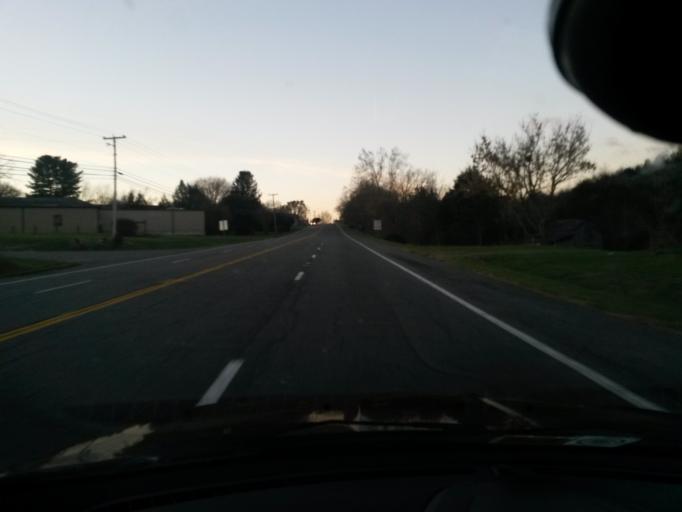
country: US
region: Virginia
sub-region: Botetourt County
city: Fincastle
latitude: 37.5043
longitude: -79.8774
